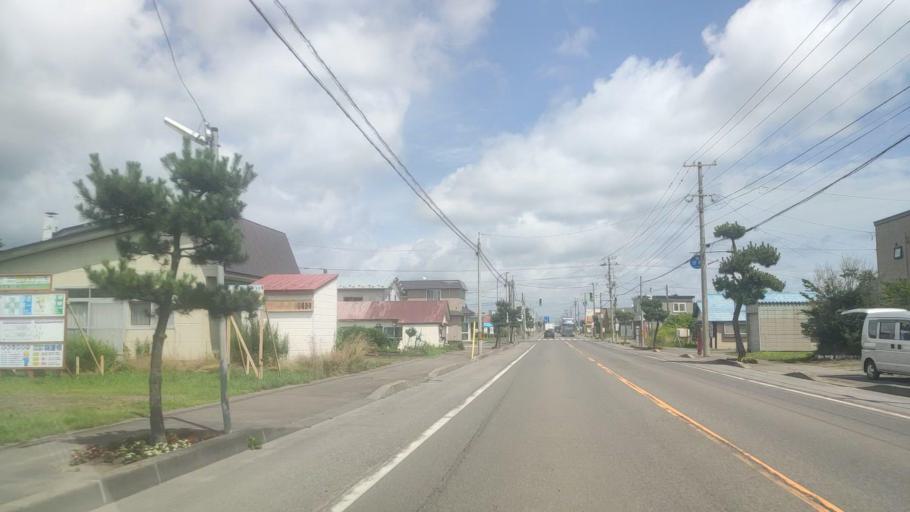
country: JP
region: Hokkaido
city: Niseko Town
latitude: 42.4353
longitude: 140.3210
